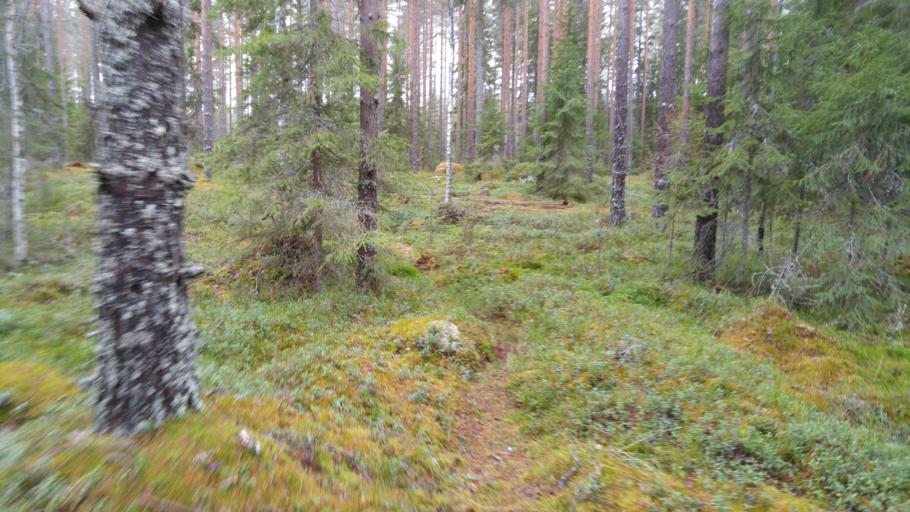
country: FI
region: Pirkanmaa
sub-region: Tampere
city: Kangasala
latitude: 61.6067
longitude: 23.9788
